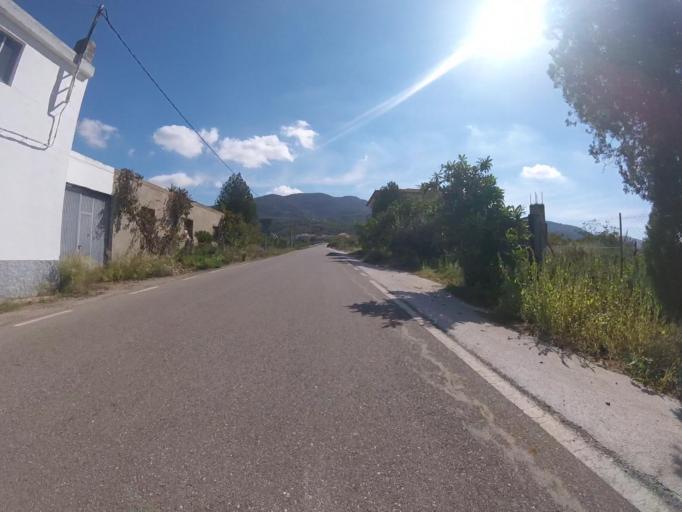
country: ES
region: Valencia
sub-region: Provincia de Castello
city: Sierra-Engarceran
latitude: 40.2976
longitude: -0.0459
